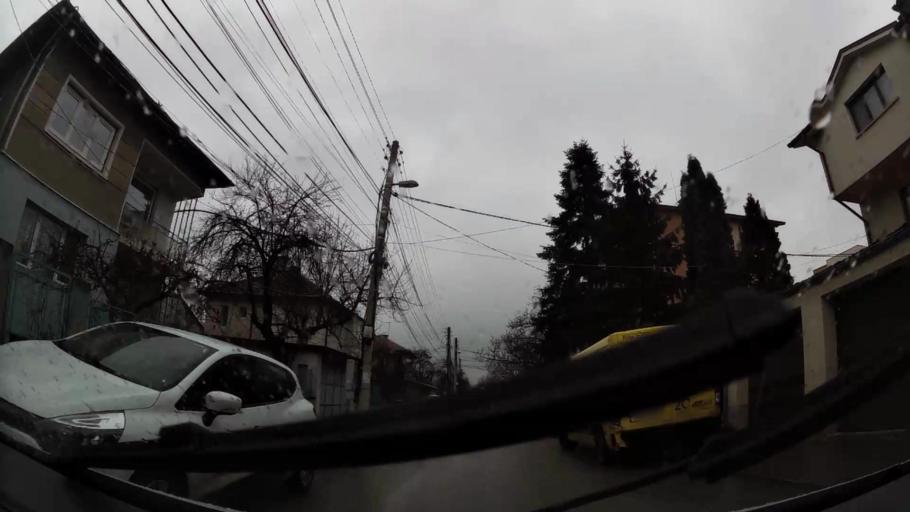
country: BG
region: Sofia-Capital
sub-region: Stolichna Obshtina
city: Sofia
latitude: 42.6329
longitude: 23.4119
